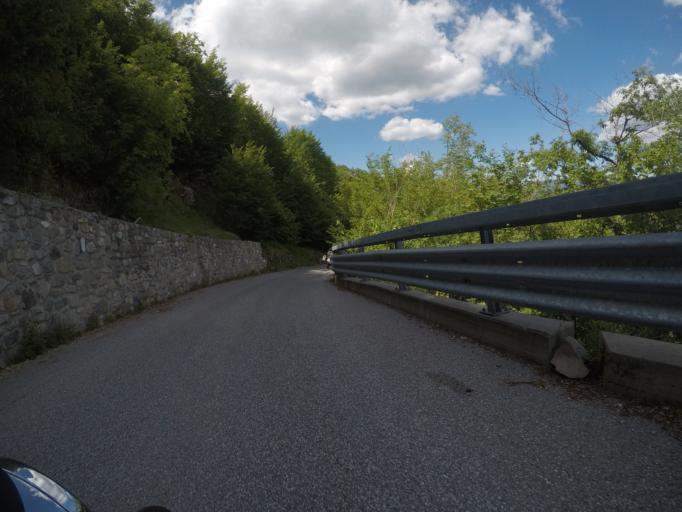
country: IT
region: Tuscany
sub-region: Provincia di Lucca
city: Minucciano
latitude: 44.1581
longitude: 10.2001
